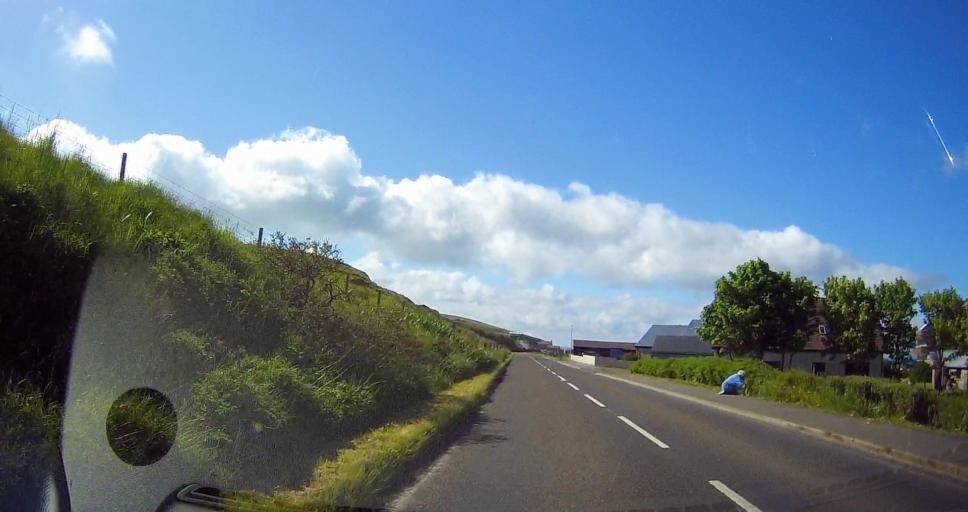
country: GB
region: Scotland
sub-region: Orkney Islands
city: Orkney
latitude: 58.9621
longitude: -2.9684
